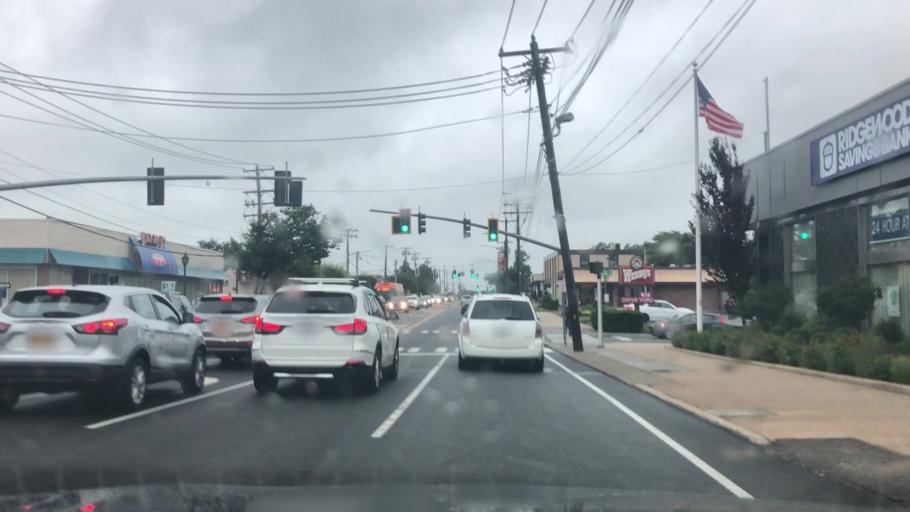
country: US
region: New York
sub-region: Nassau County
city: Franklin Square
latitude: 40.7076
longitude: -73.6772
